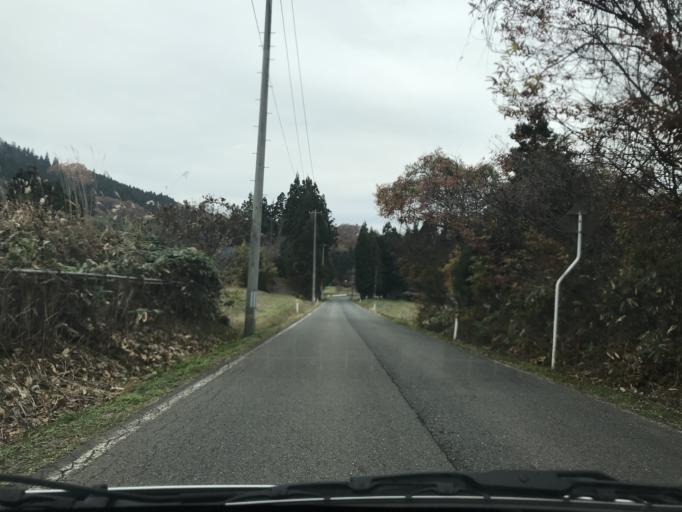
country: JP
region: Iwate
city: Kitakami
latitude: 39.2867
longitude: 141.1762
